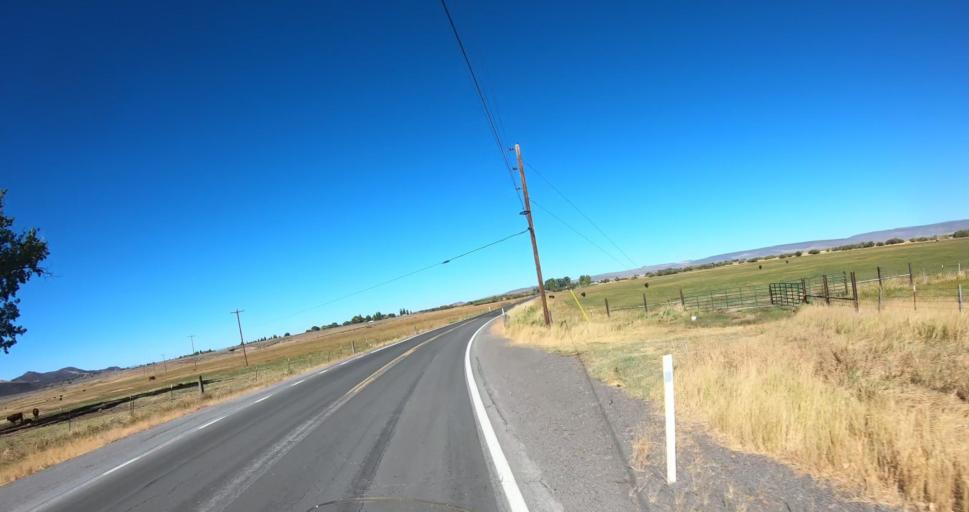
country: US
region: Oregon
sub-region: Lake County
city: Lakeview
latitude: 42.6755
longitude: -120.5279
